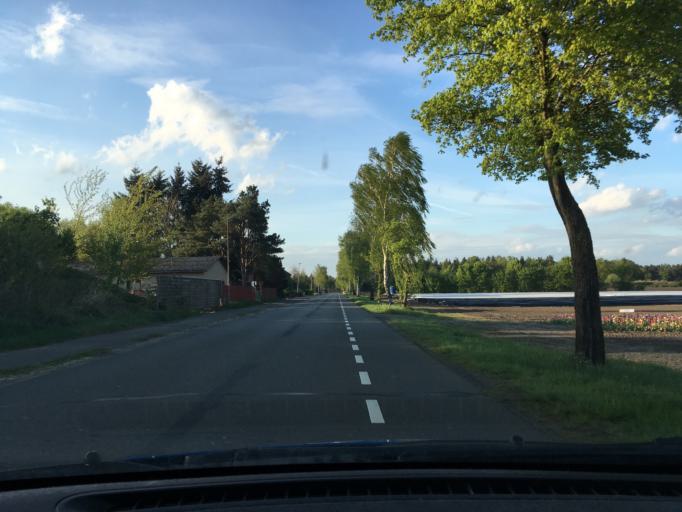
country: DE
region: Lower Saxony
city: Wietzendorf
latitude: 52.9267
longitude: 9.9797
